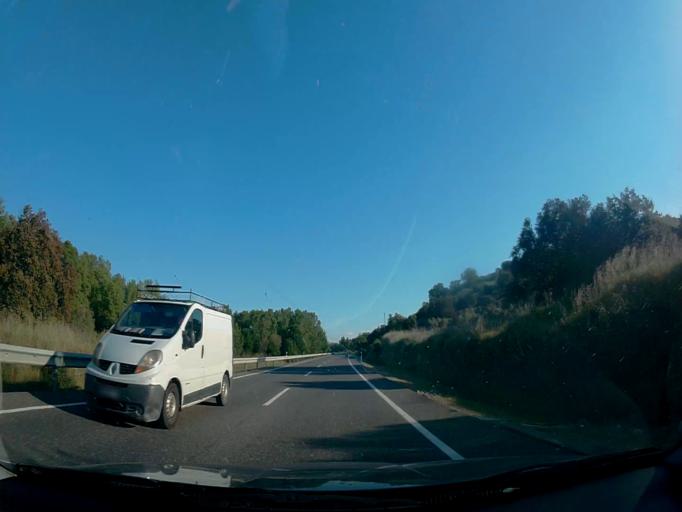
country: ES
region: Castille-La Mancha
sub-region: Province of Toledo
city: Escalona
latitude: 40.1790
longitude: -4.3993
